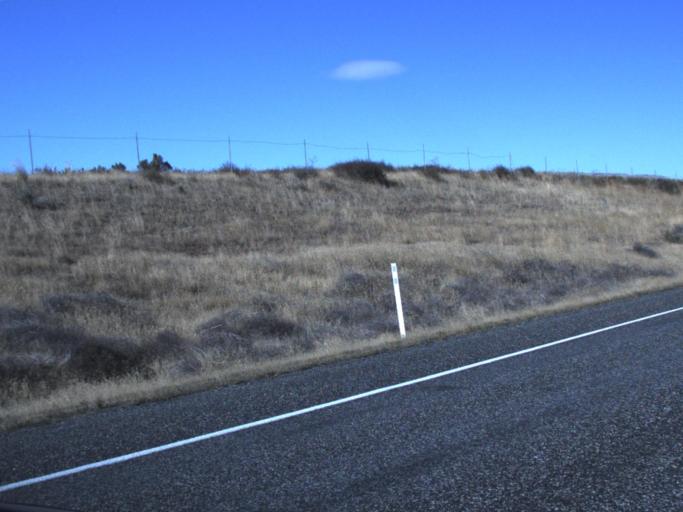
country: US
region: Washington
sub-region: Benton County
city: West Richland
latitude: 46.3639
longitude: -119.3872
